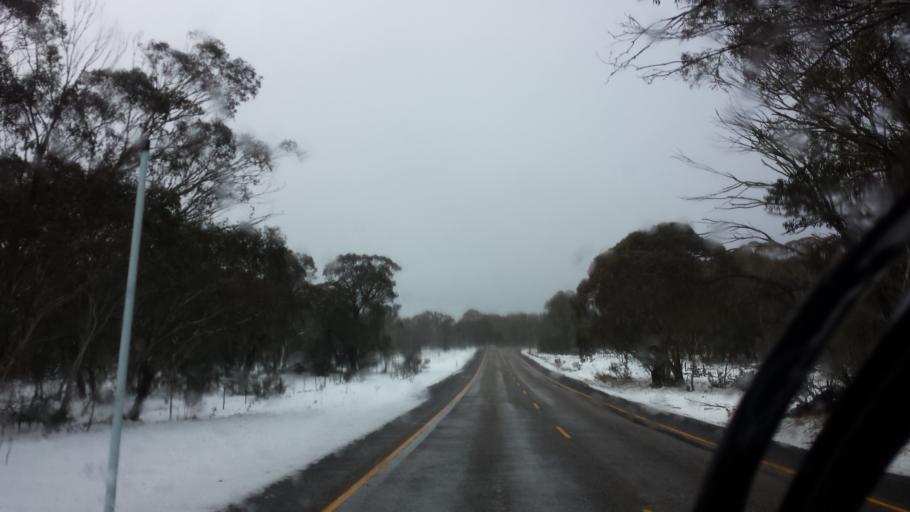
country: AU
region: Victoria
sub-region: Alpine
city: Mount Beauty
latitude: -37.0292
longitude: 147.2924
